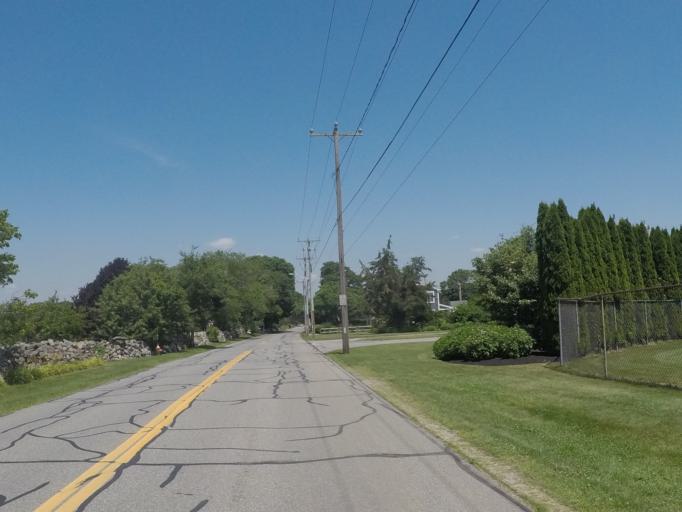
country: US
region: Massachusetts
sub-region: Bristol County
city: Bliss Corner
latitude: 41.5448
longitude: -70.9543
